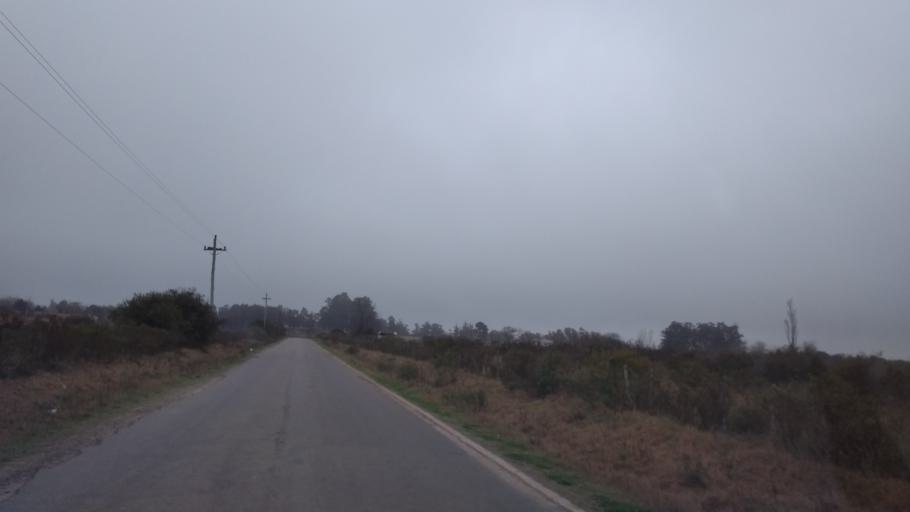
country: UY
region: Florida
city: Florida
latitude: -34.0844
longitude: -56.2057
